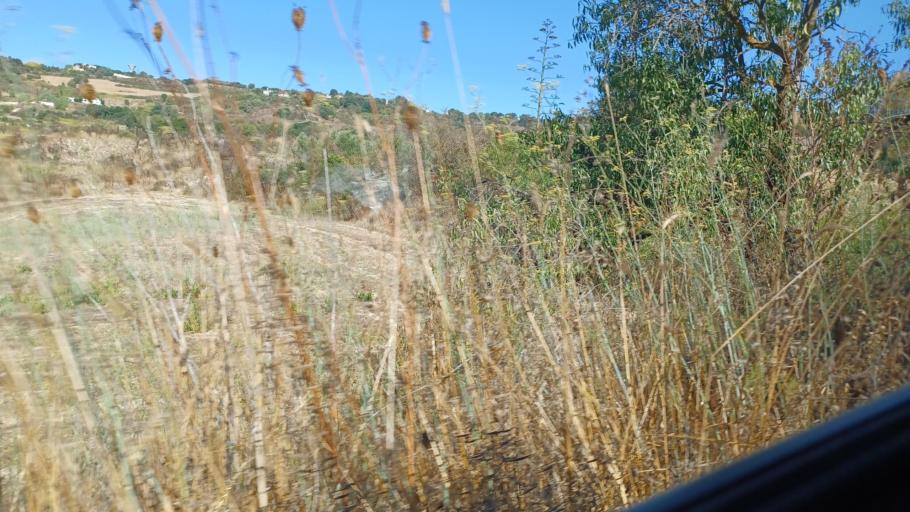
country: CY
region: Pafos
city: Mesogi
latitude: 34.8751
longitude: 32.5147
